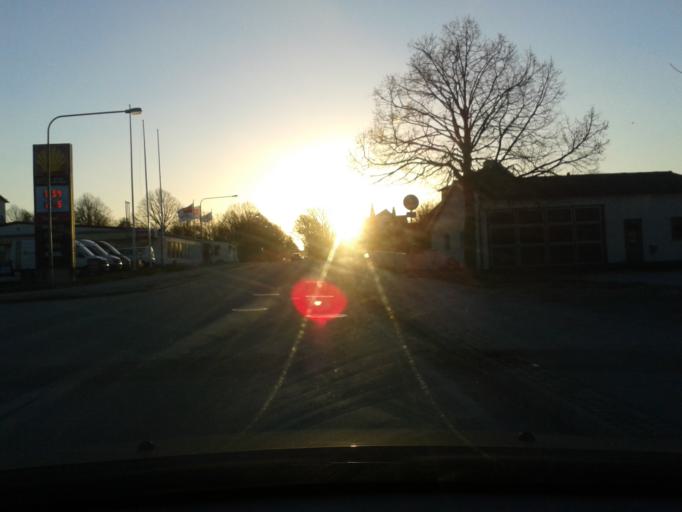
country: SE
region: Gotland
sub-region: Gotland
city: Visby
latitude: 57.6299
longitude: 18.2863
